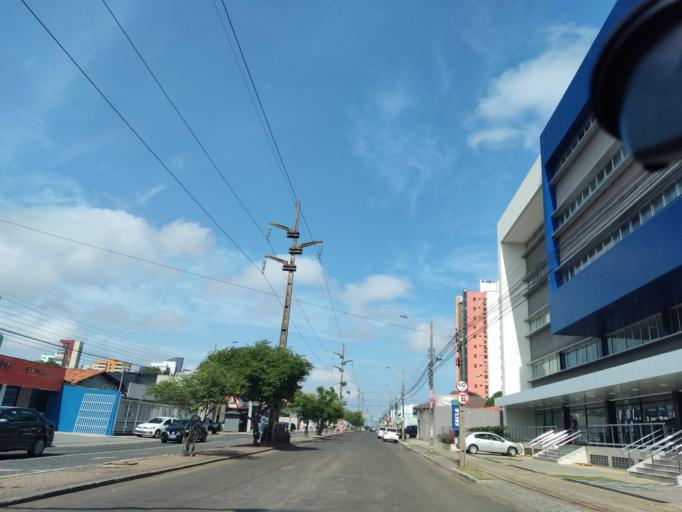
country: BR
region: Piaui
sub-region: Teresina
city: Teresina
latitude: -5.0703
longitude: -42.7818
